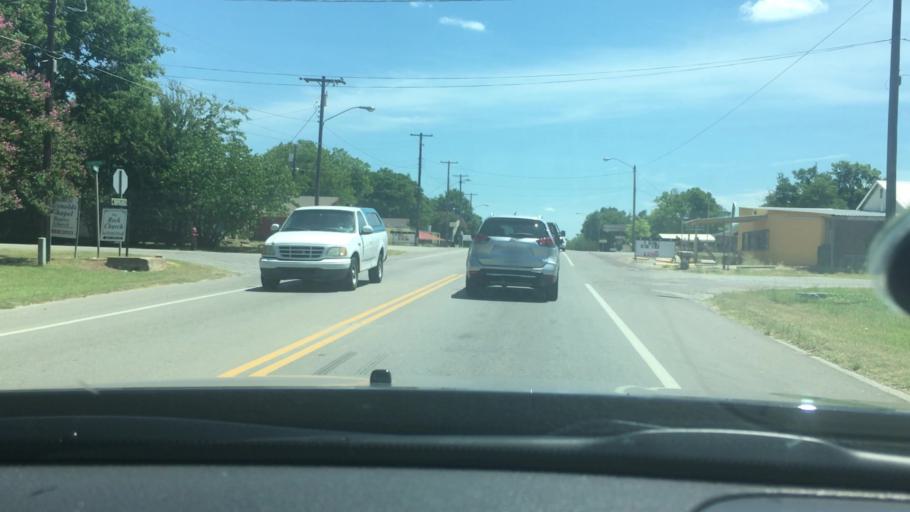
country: US
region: Oklahoma
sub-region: Bryan County
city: Durant
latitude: 34.0166
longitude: -96.1372
